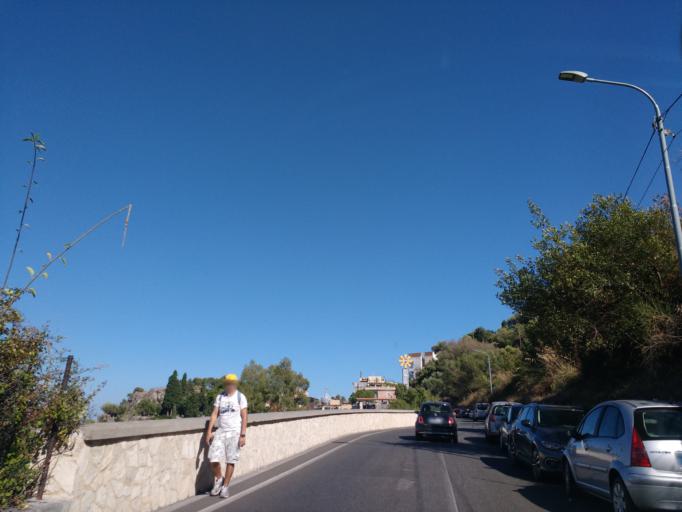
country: IT
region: Sicily
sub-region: Messina
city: Taormina
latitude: 37.8581
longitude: 15.2984
